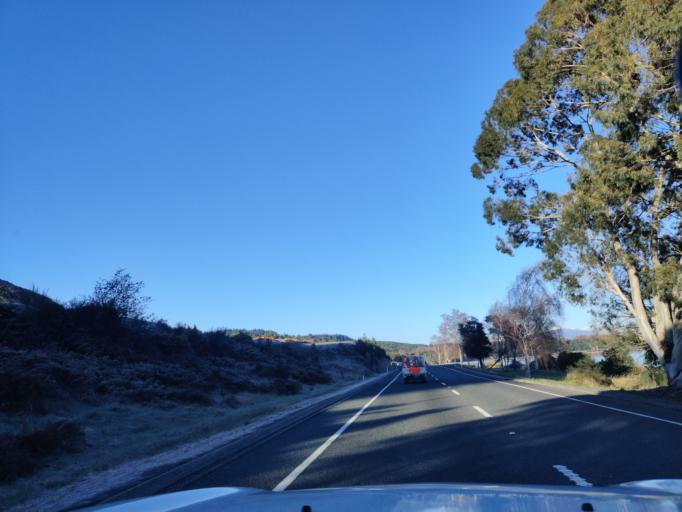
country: NZ
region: Waikato
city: Turangi
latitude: -38.8967
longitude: 175.9466
